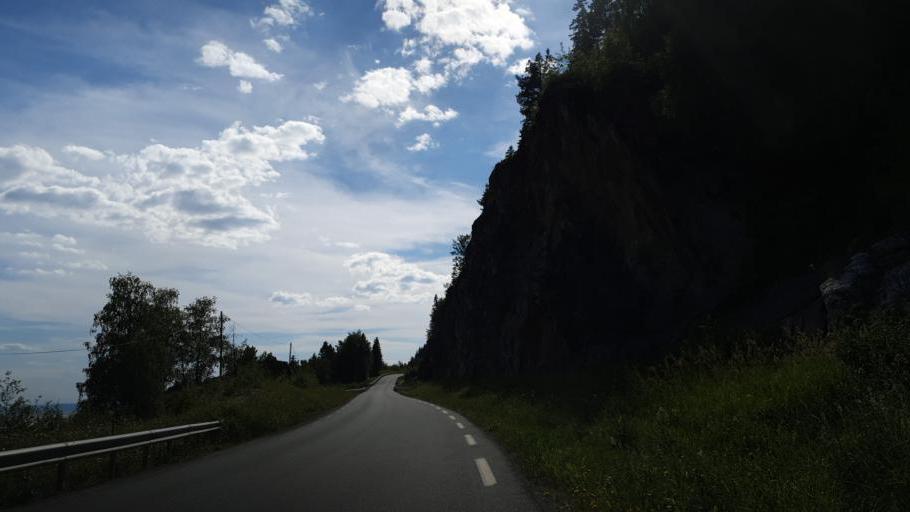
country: NO
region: Nord-Trondelag
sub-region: Leksvik
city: Leksvik
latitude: 63.6203
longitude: 10.5260
